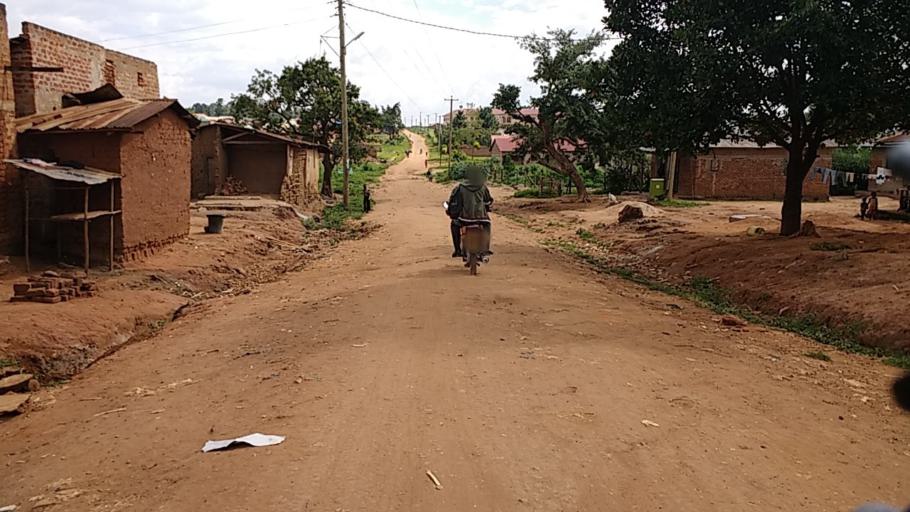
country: UG
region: Eastern Region
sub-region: Mbale District
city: Mbale
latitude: 1.0850
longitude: 34.1630
